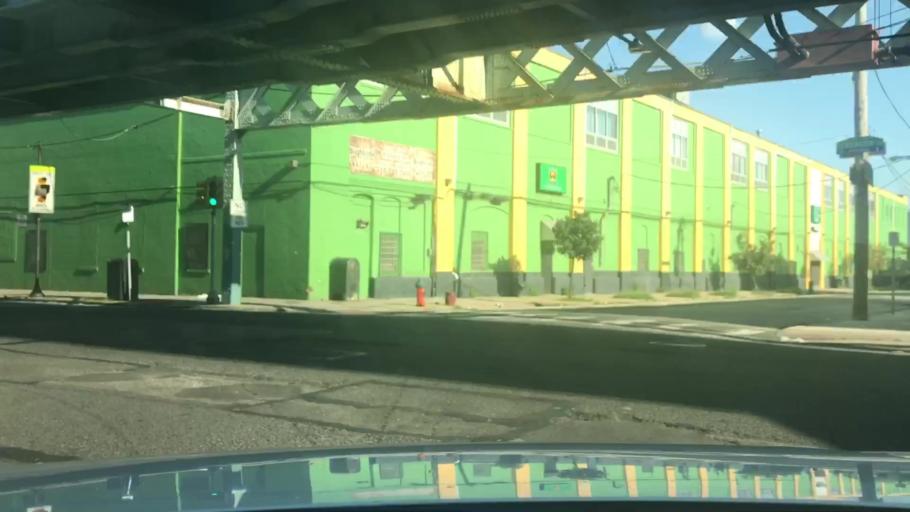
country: US
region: Pennsylvania
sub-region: Philadelphia County
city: Philadelphia
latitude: 39.9876
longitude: -75.1298
